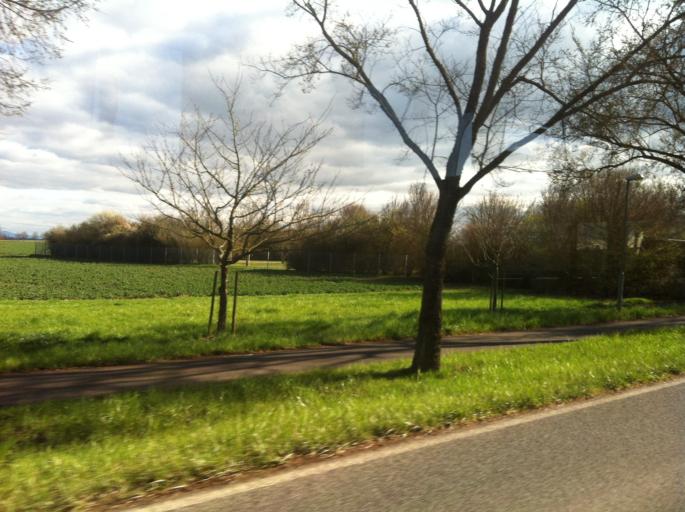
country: DE
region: Hesse
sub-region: Regierungsbezirk Darmstadt
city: Hochheim am Main
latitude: 50.0283
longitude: 8.3664
